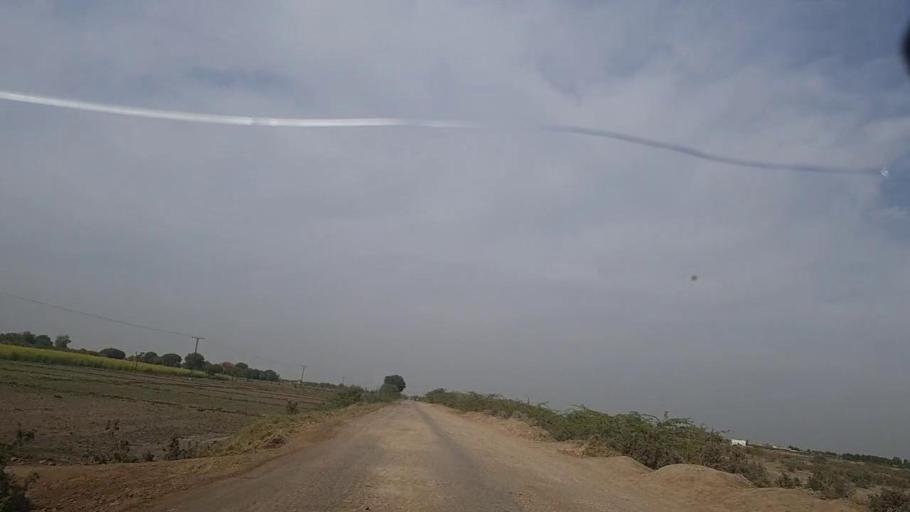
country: PK
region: Sindh
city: Pithoro
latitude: 25.5560
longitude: 69.3628
